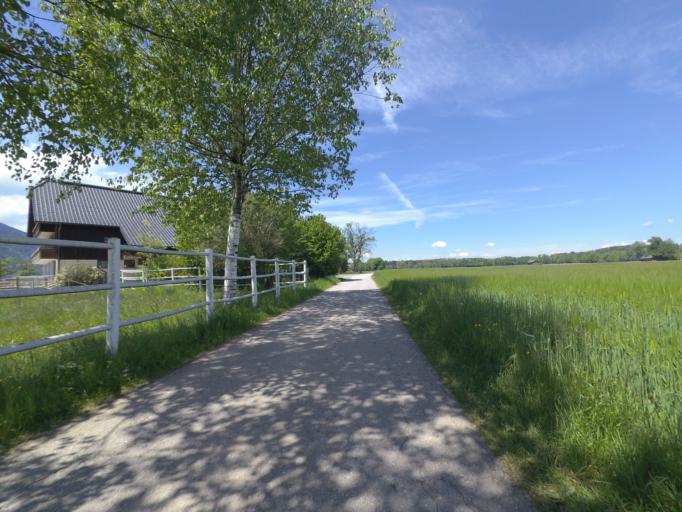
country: AT
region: Salzburg
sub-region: Politischer Bezirk Salzburg-Umgebung
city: Anif
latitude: 47.7536
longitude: 13.0590
